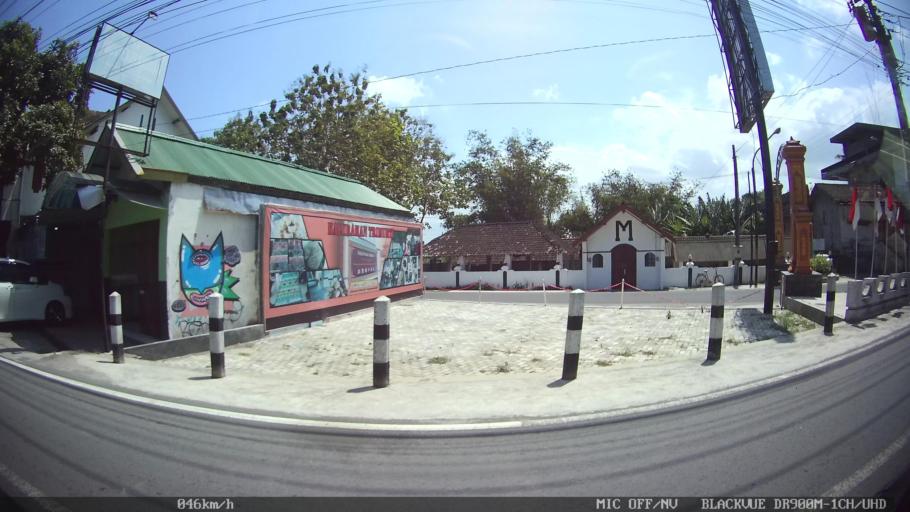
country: ID
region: Daerah Istimewa Yogyakarta
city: Srandakan
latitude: -7.9318
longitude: 110.2650
